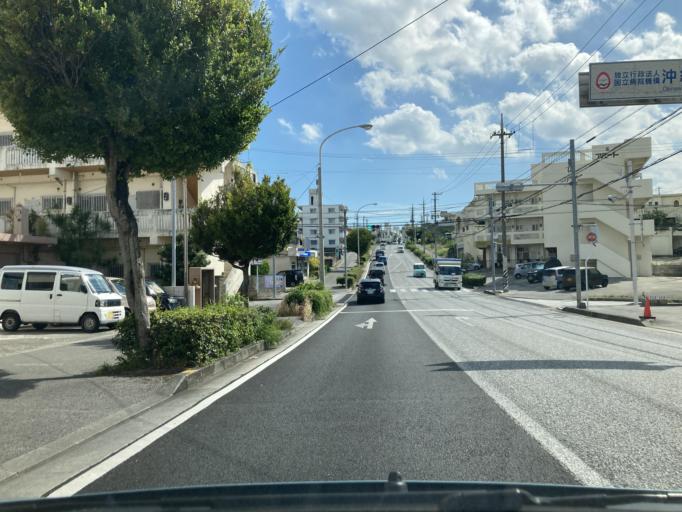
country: JP
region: Okinawa
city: Ginowan
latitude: 26.2530
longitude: 127.7571
